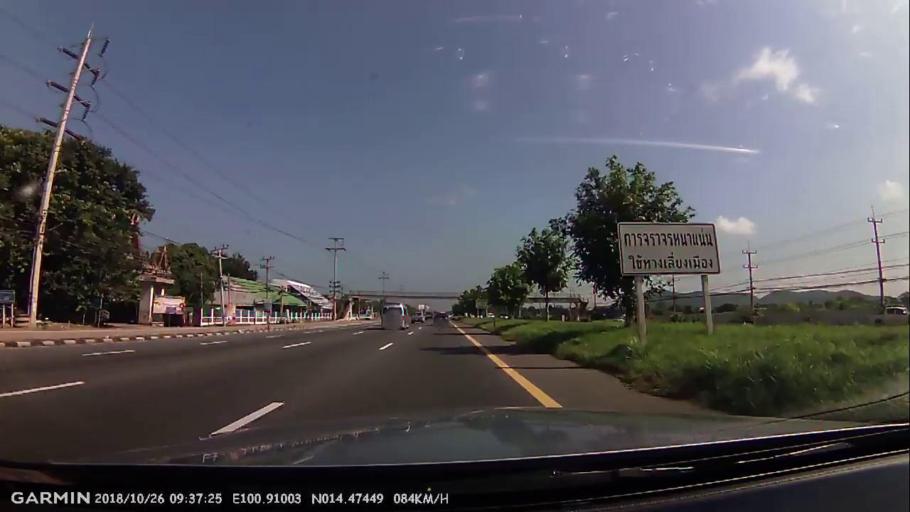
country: TH
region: Sara Buri
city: Saraburi
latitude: 14.4747
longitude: 100.9101
